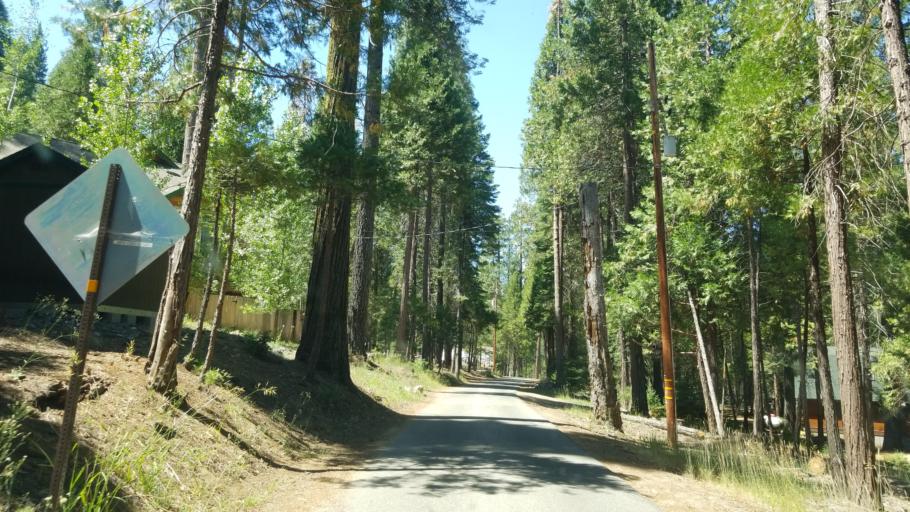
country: US
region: California
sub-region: Madera County
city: Ahwahnee
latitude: 37.5430
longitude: -119.6437
